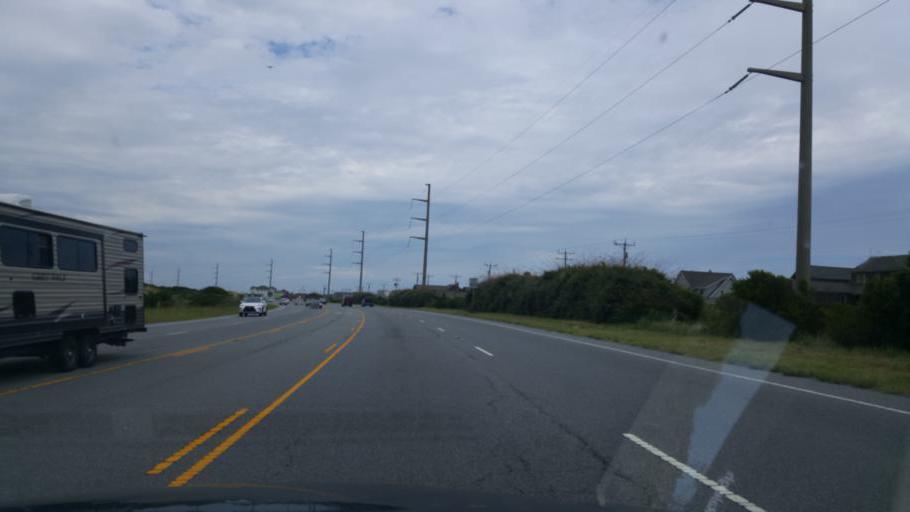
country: US
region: North Carolina
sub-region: Dare County
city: Nags Head
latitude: 35.9605
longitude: -75.6264
